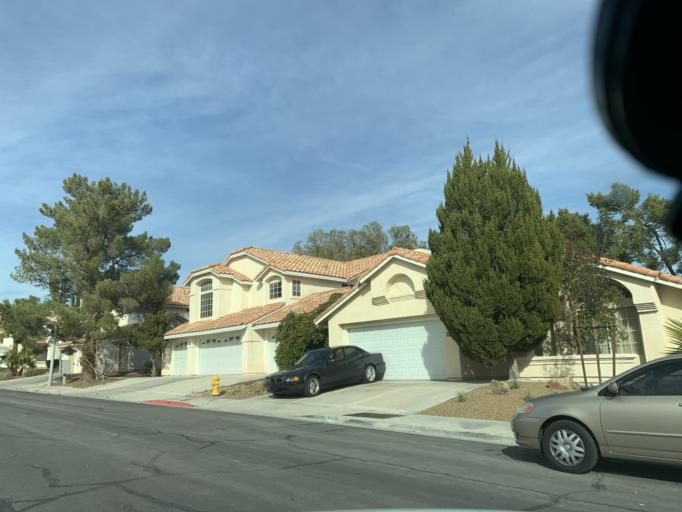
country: US
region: Nevada
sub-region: Clark County
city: Summerlin South
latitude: 36.1498
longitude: -115.3022
